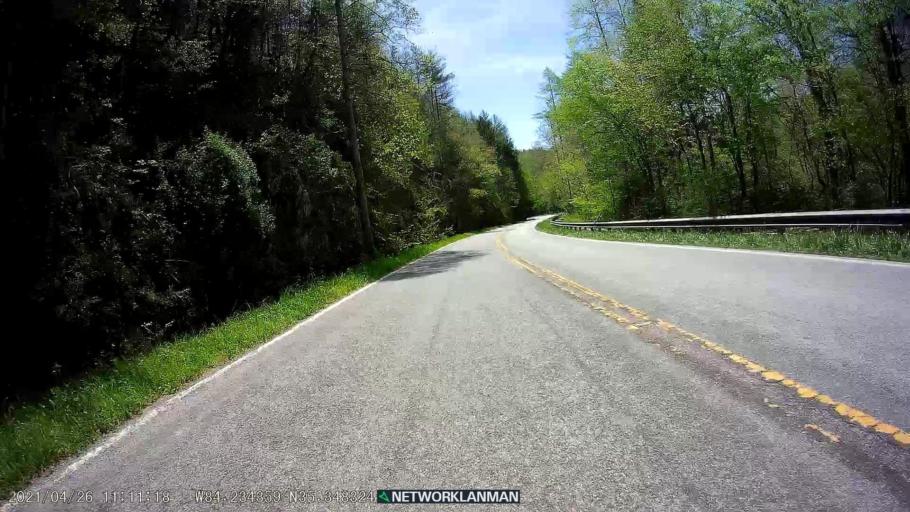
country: US
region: Tennessee
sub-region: Monroe County
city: Madisonville
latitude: 35.3485
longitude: -84.2342
